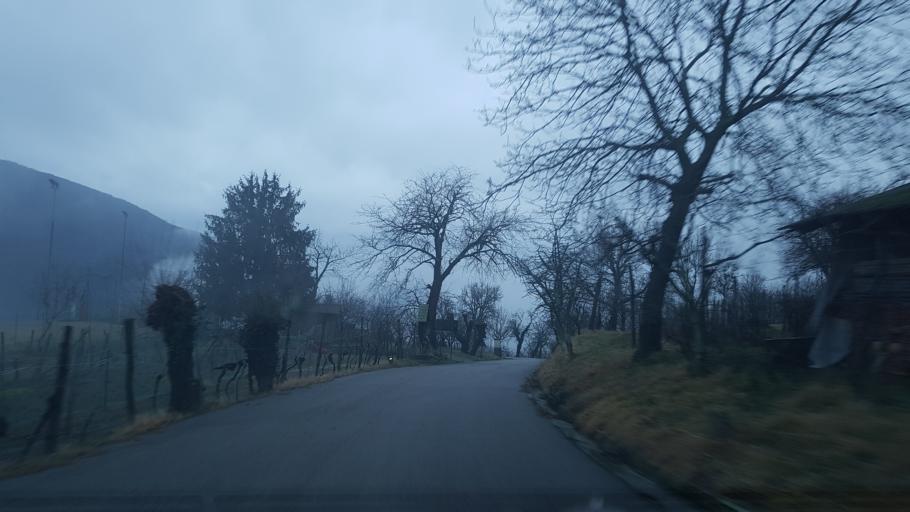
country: IT
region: Friuli Venezia Giulia
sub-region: Provincia di Udine
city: San Leonardo
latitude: 46.0896
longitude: 13.5488
